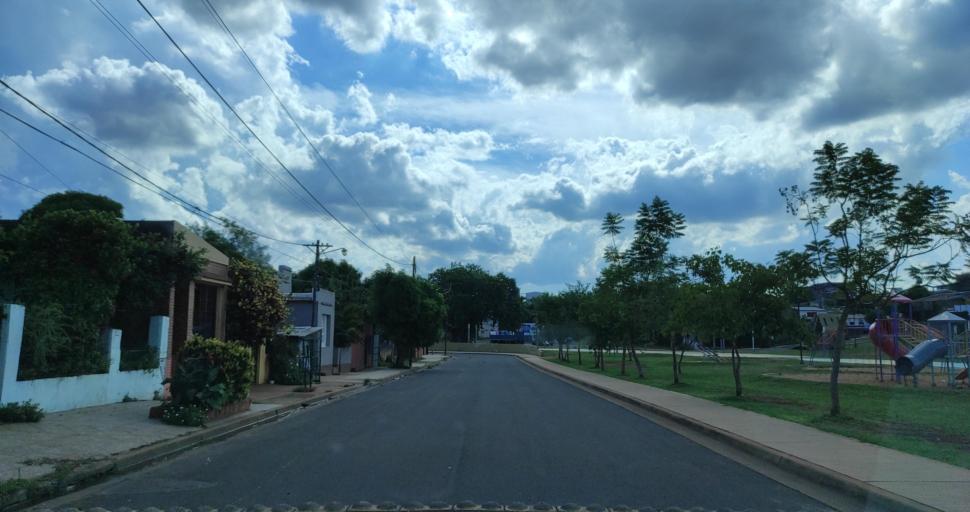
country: AR
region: Misiones
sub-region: Departamento de Capital
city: Posadas
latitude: -27.3797
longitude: -55.8889
